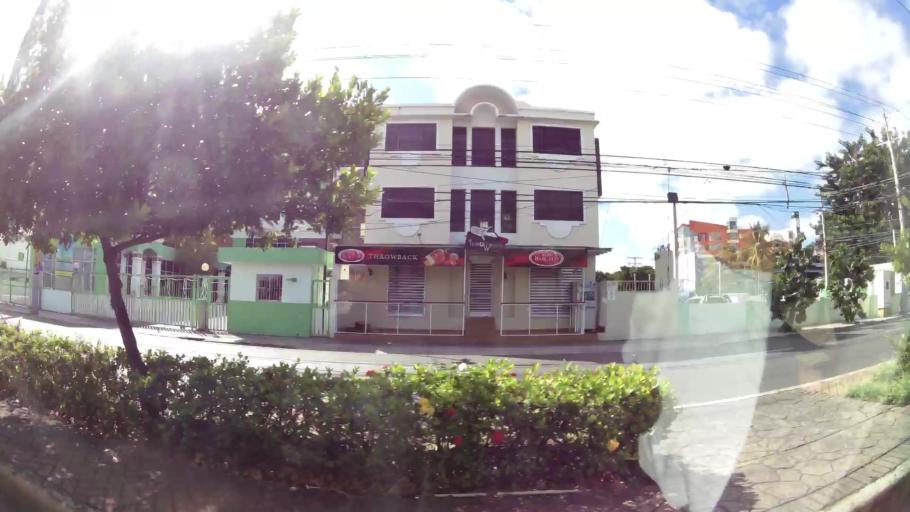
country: DO
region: Nacional
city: La Julia
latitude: 18.4590
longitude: -69.9365
